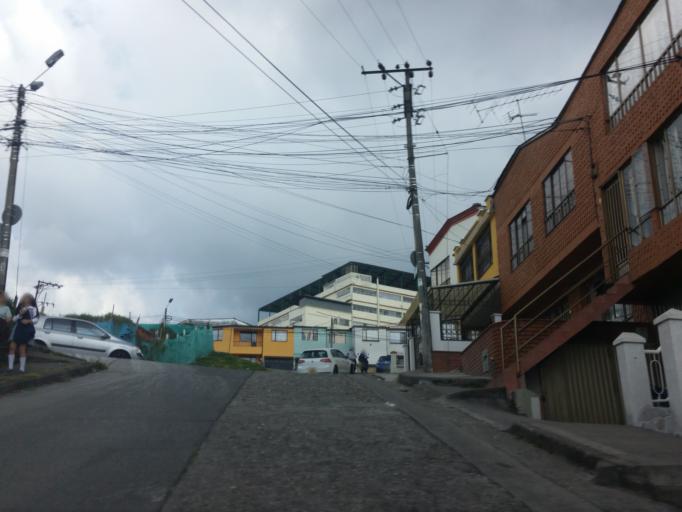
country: CO
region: Caldas
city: Manizales
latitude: 5.0598
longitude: -75.5018
